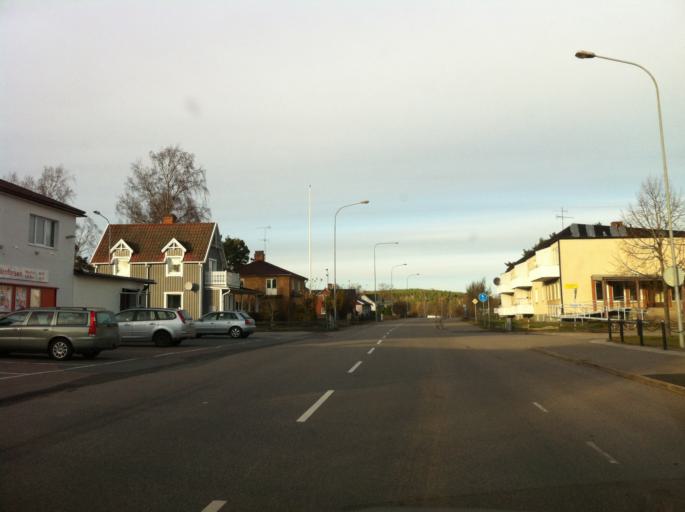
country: SE
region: Kalmar
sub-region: Hultsfreds Kommun
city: Virserum
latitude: 57.4046
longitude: 15.6115
